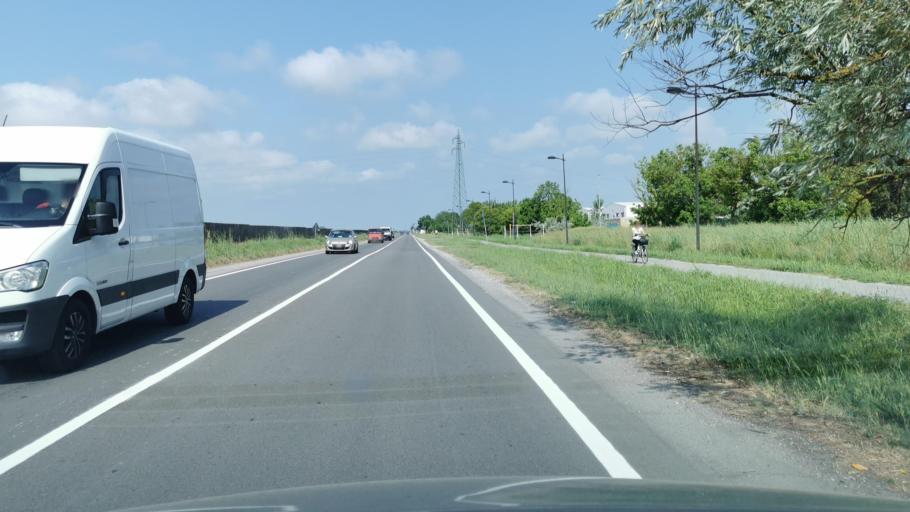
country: IT
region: Emilia-Romagna
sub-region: Provincia di Ferrara
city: Porto Garibaldi
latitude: 44.6764
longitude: 12.2199
